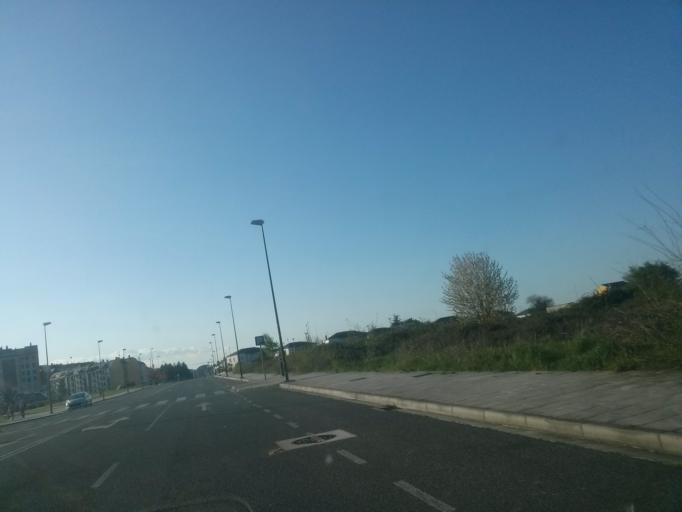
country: ES
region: Galicia
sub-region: Provincia de Lugo
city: Lugo
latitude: 42.9999
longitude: -7.5396
